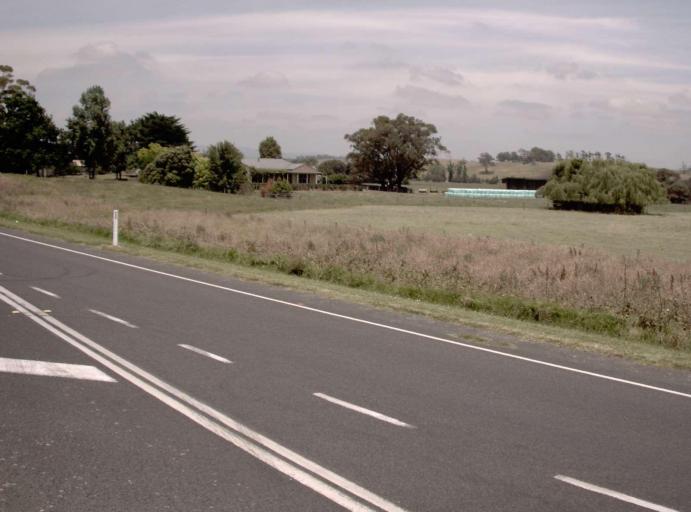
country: AU
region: Victoria
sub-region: Latrobe
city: Traralgon
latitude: -38.2095
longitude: 146.5450
